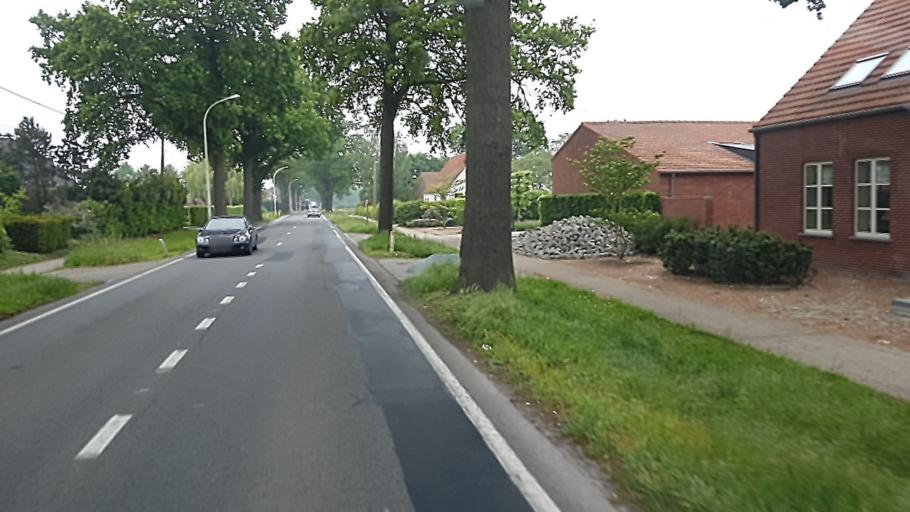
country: BE
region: Flanders
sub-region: Provincie Antwerpen
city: Brecht
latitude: 51.3582
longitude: 4.6237
